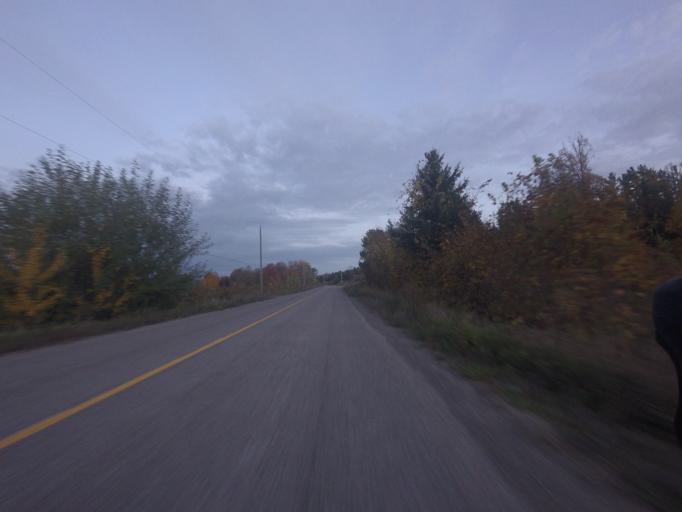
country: CA
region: Ontario
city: Renfrew
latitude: 45.3464
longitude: -76.9365
